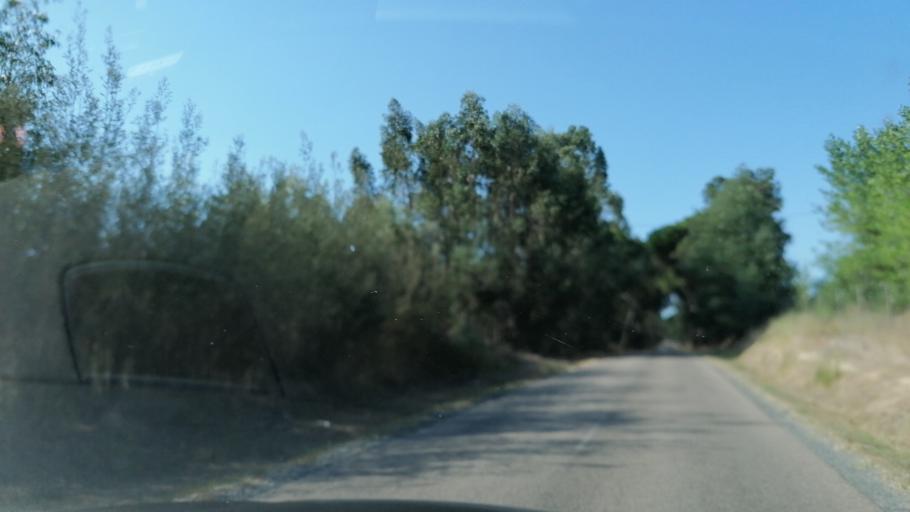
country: PT
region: Santarem
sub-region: Coruche
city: Coruche
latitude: 38.8017
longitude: -8.5789
